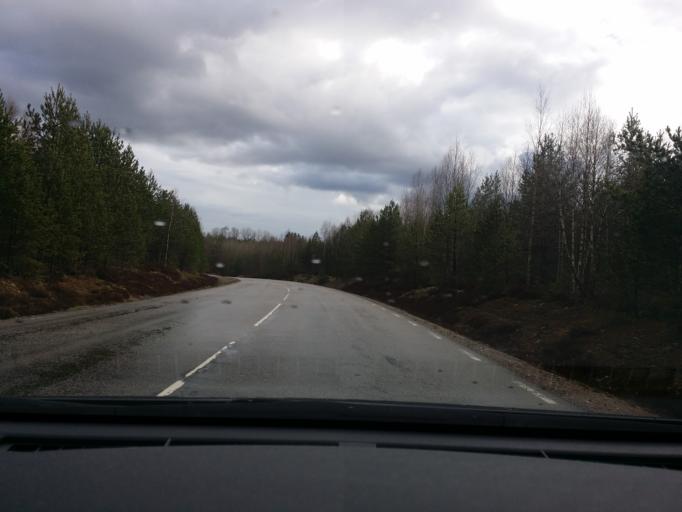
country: SE
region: Soedermanland
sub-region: Eskilstuna Kommun
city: Arla
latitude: 59.3224
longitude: 16.6799
